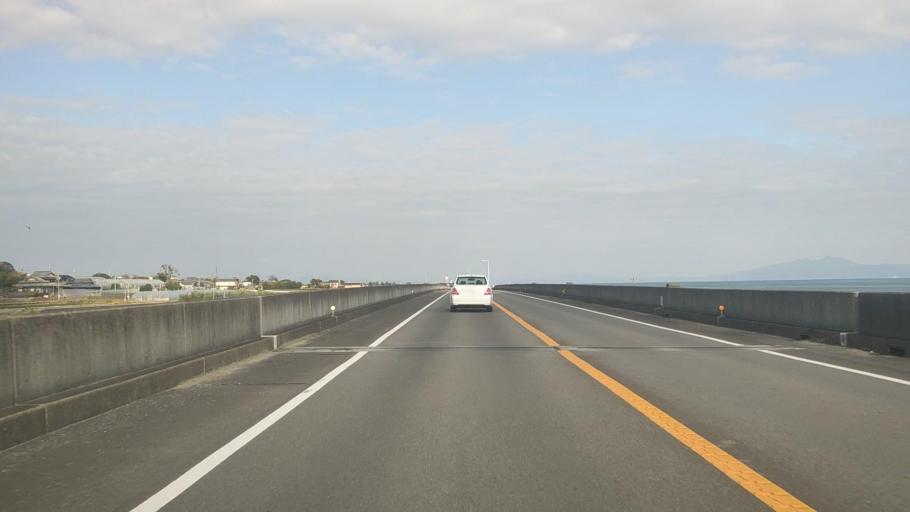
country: JP
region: Nagasaki
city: Shimabara
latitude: 32.7237
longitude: 130.3609
